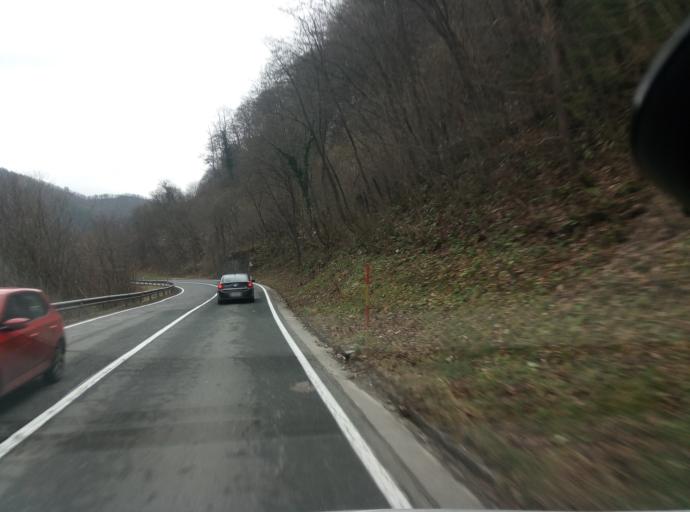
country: SI
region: Zagorje ob Savi
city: Zagorje ob Savi
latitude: 46.1140
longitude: 14.9838
